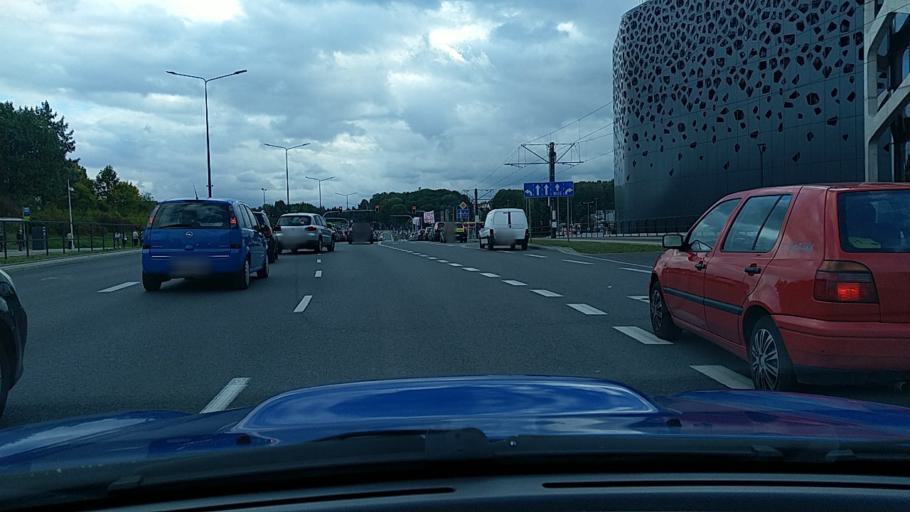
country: PL
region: Warmian-Masurian Voivodeship
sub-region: Powiat olsztynski
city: Olsztyn
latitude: 53.7543
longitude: 20.4861
